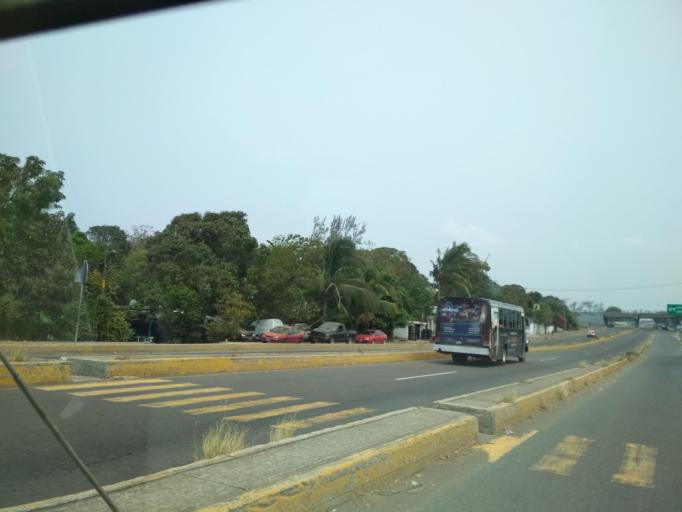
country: MX
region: Veracruz
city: Paso del Toro
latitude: 19.0270
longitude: -96.1367
